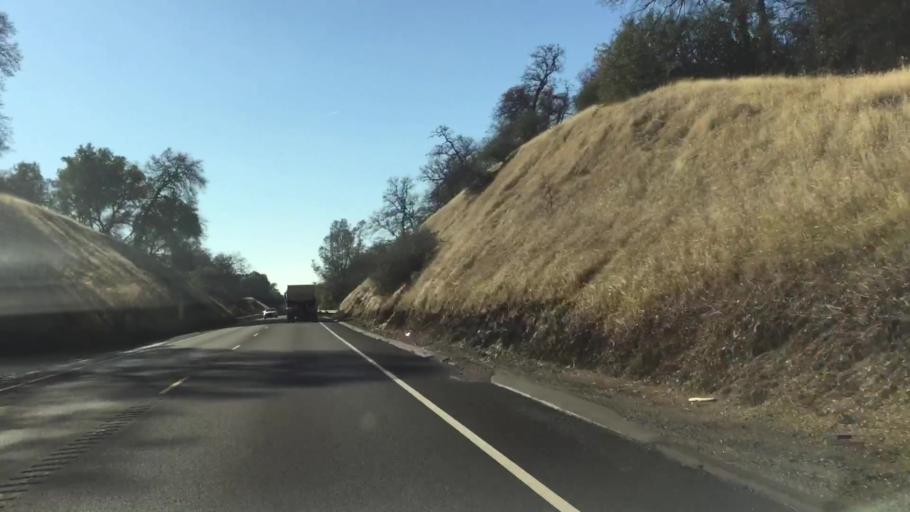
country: US
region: California
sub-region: Butte County
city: Paradise
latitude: 39.6432
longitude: -121.5697
